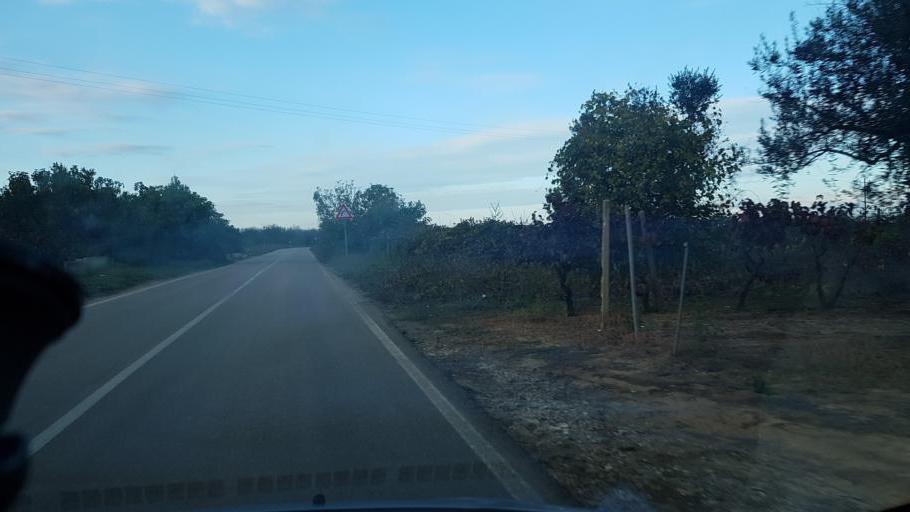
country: IT
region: Apulia
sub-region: Provincia di Lecce
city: Guagnano
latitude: 40.4277
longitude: 17.9498
